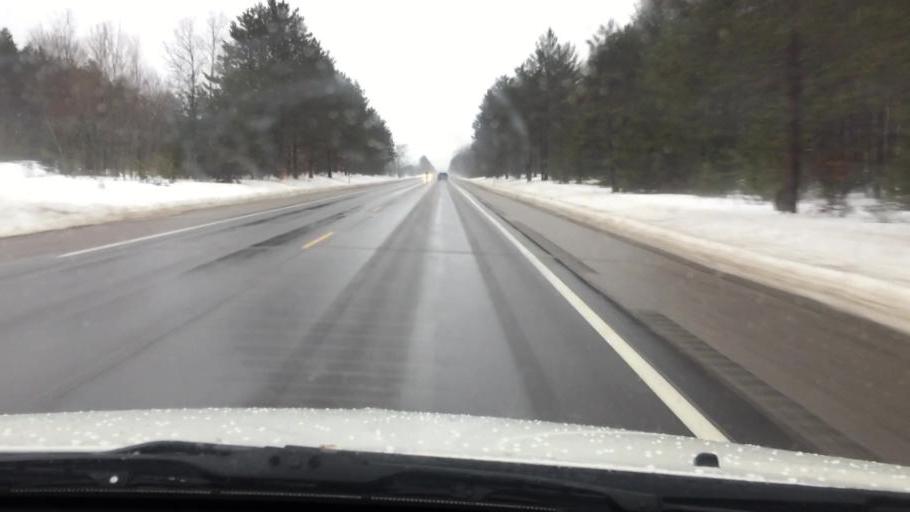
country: US
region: Michigan
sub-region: Kalkaska County
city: Kalkaska
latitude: 44.6933
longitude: -85.2125
